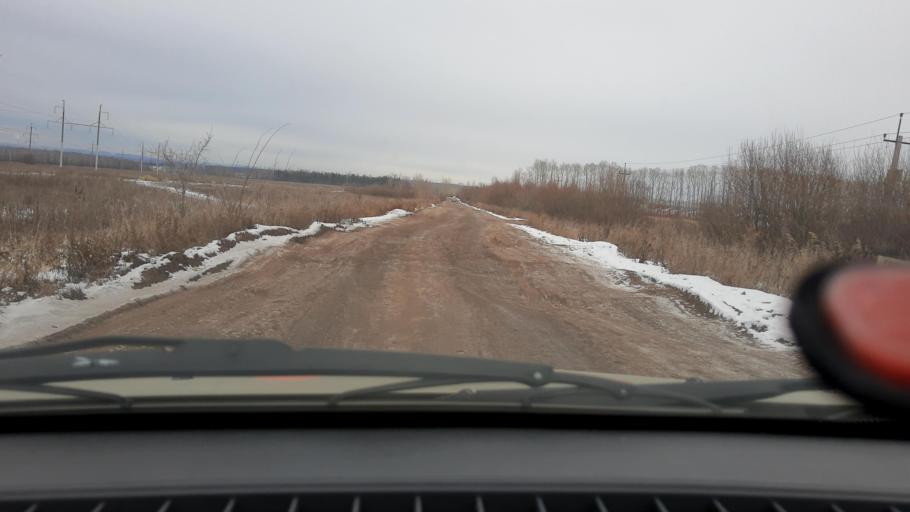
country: RU
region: Bashkortostan
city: Kabakovo
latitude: 54.6372
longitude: 56.1004
